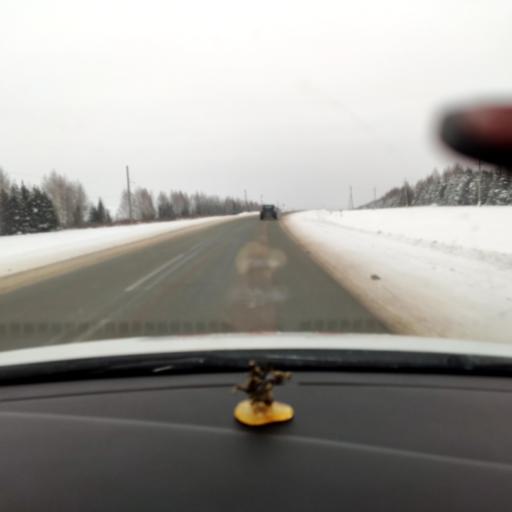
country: RU
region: Tatarstan
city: Vysokaya Gora
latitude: 56.0274
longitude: 49.2517
